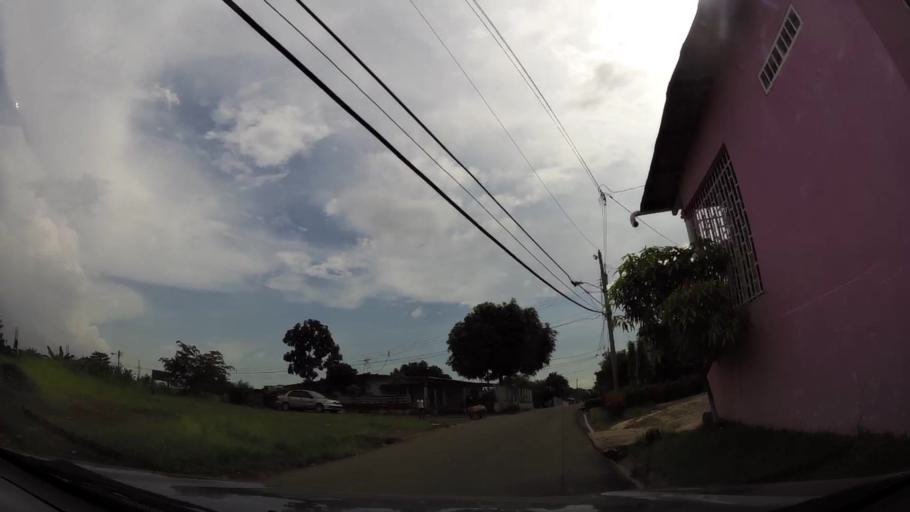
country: PA
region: Panama
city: Tocumen
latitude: 9.1008
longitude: -79.3669
